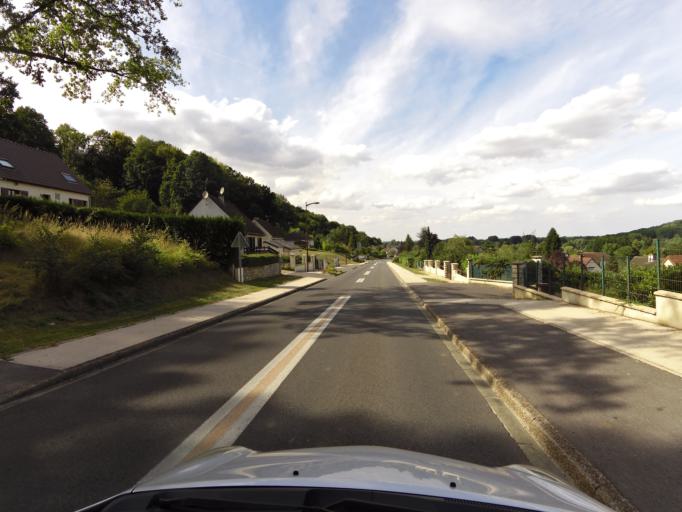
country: FR
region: Picardie
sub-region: Departement de l'Aisne
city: Bruyeres-et-Montberault
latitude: 49.5174
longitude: 3.6674
